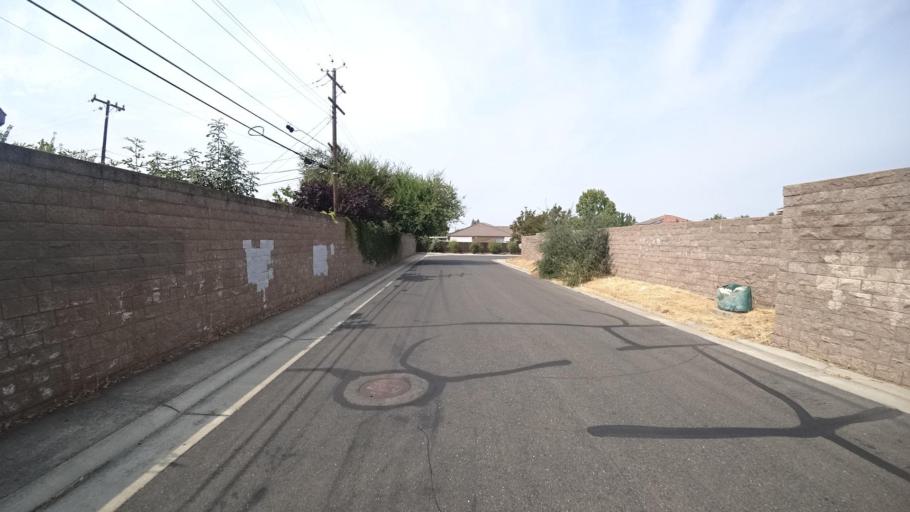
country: US
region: California
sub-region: Sacramento County
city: Elk Grove
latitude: 38.4198
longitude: -121.3733
